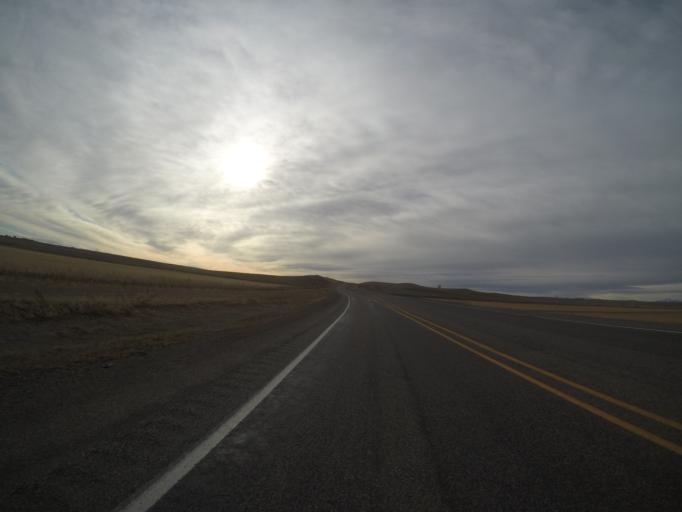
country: US
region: Montana
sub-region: Yellowstone County
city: Laurel
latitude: 45.6098
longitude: -108.8216
